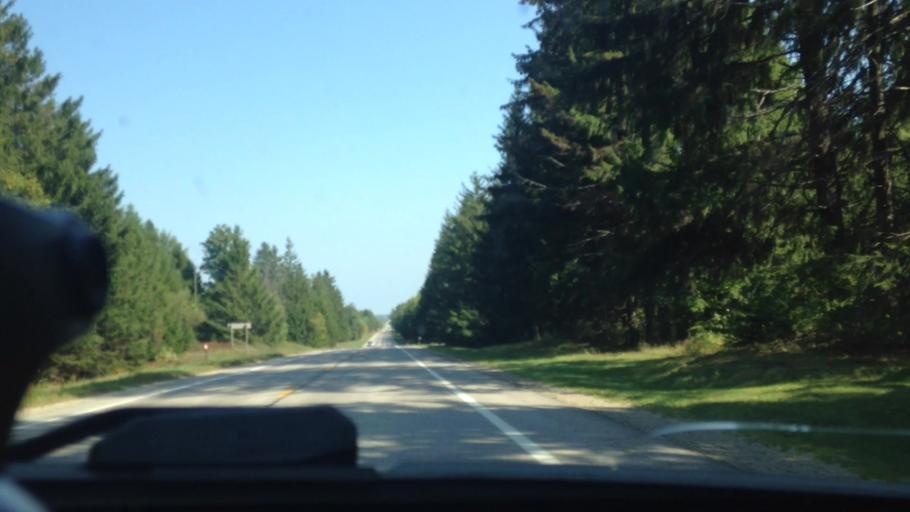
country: US
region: Michigan
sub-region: Luce County
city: Newberry
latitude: 46.3037
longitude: -85.4349
